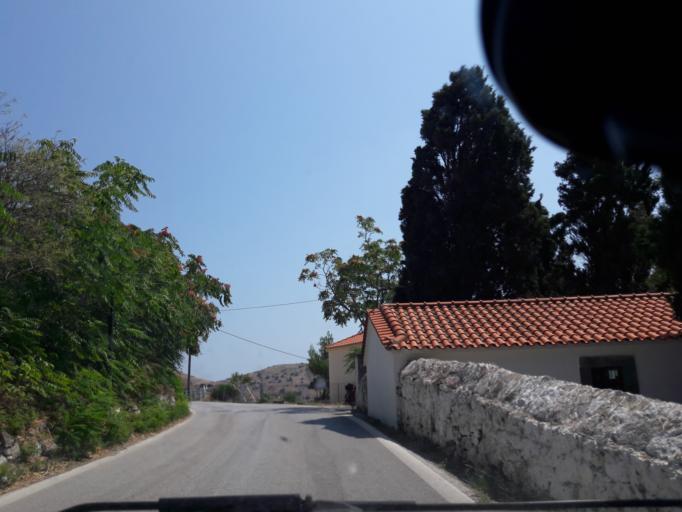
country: GR
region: North Aegean
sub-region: Nomos Lesvou
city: Myrina
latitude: 39.8576
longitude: 25.0842
